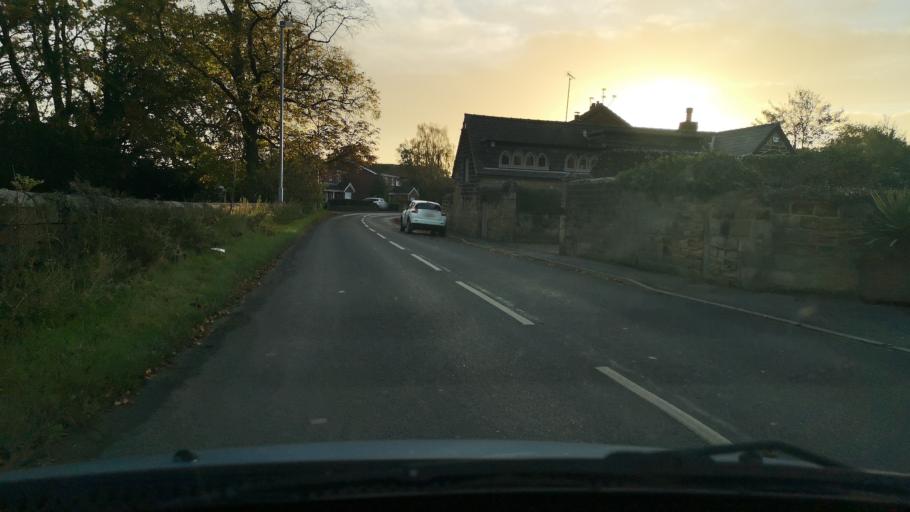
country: GB
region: England
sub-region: City and Borough of Wakefield
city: Low Ackworth
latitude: 53.6507
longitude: -1.3269
